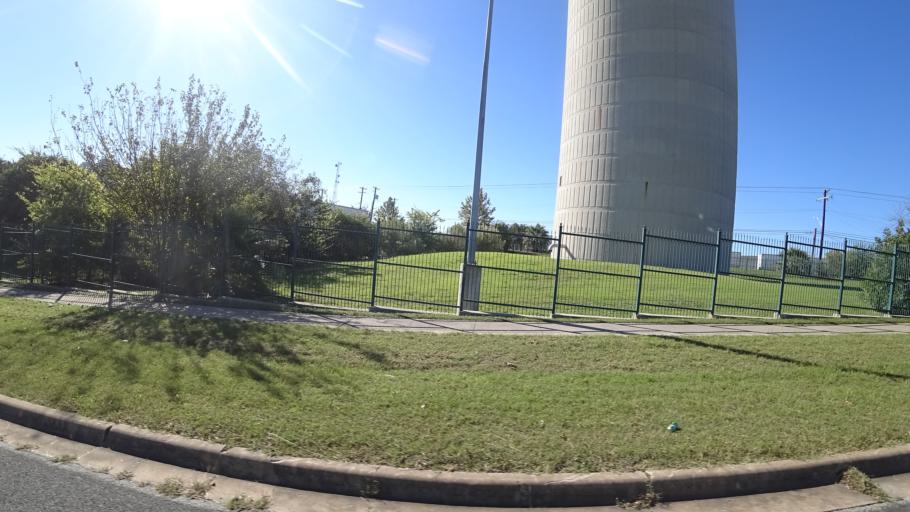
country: US
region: Texas
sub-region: Travis County
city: Austin
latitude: 30.3014
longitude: -97.6934
